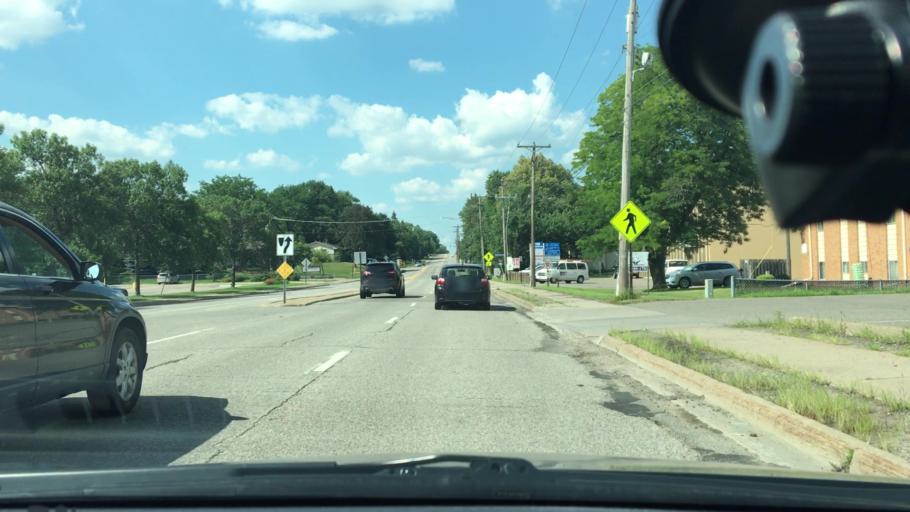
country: US
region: Minnesota
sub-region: Hennepin County
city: New Hope
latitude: 45.0082
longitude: -93.3802
